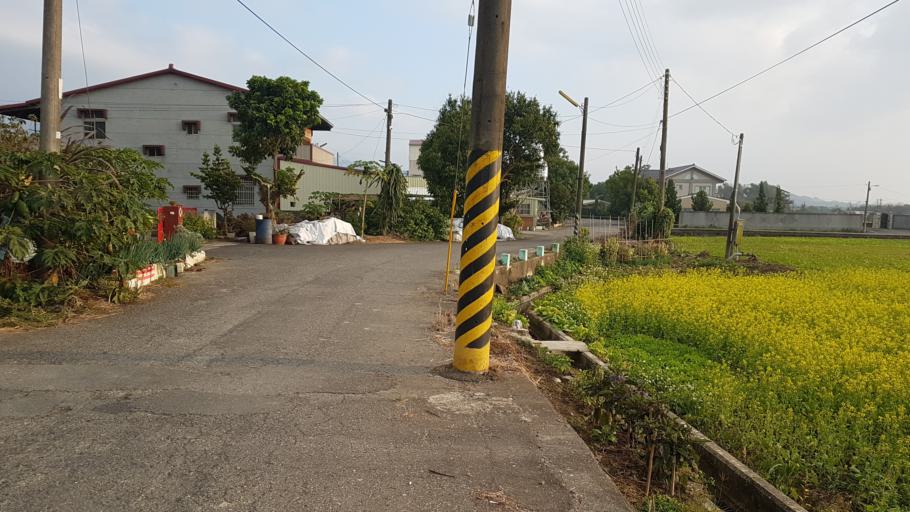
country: TW
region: Taiwan
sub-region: Chiayi
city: Jiayi Shi
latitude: 23.3716
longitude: 120.4549
